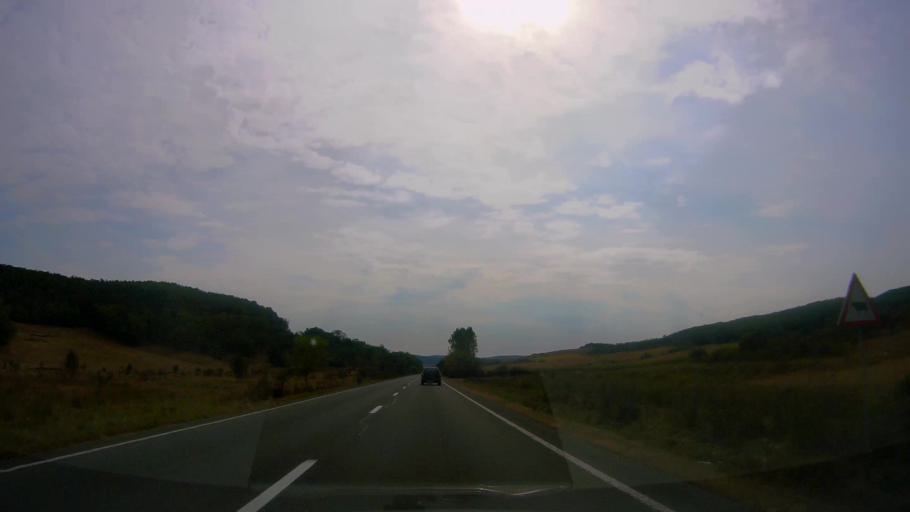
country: RO
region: Salaj
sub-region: Comuna Hida
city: Hida
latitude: 47.0524
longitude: 23.2362
